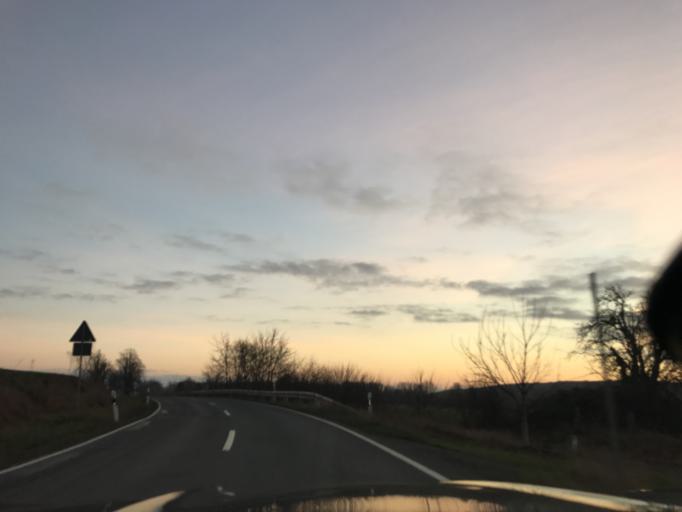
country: DE
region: Brandenburg
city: Ketzin
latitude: 52.5129
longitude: 12.8506
